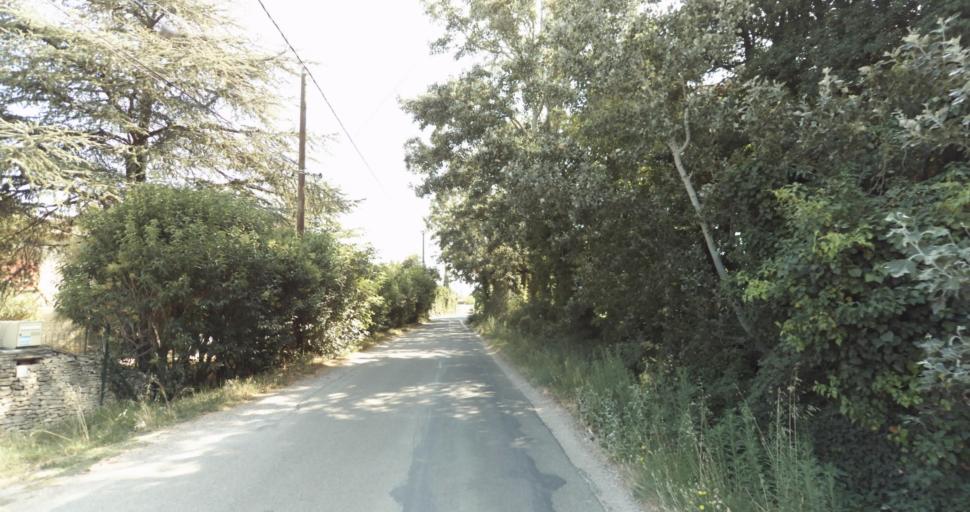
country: FR
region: Provence-Alpes-Cote d'Azur
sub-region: Departement du Vaucluse
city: Monteux
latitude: 44.0316
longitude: 5.0196
